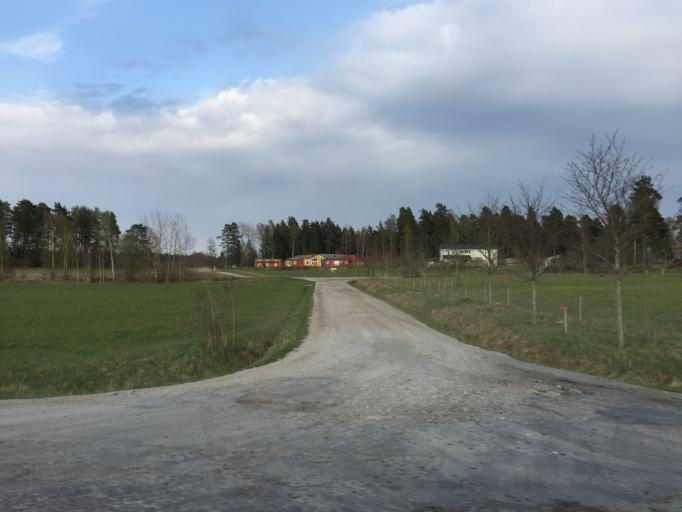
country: SE
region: Stockholm
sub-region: Sodertalje Kommun
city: Pershagen
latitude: 59.0448
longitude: 17.6053
